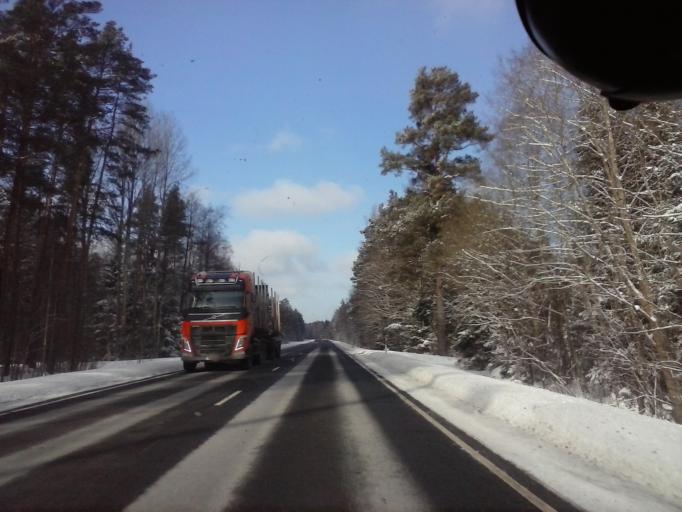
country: EE
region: Paernumaa
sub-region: Paikuse vald
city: Paikuse
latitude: 58.2450
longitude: 24.6891
